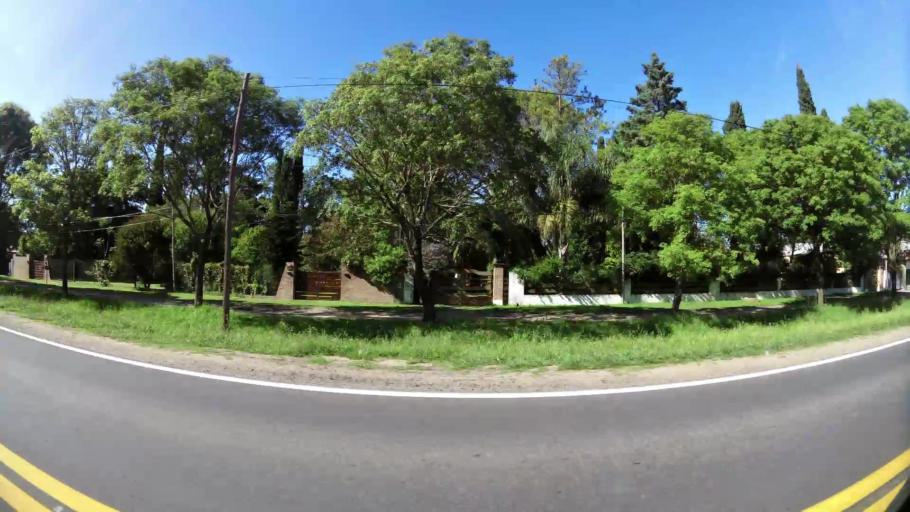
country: AR
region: Santa Fe
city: Esperanza
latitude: -31.4498
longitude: -60.9000
